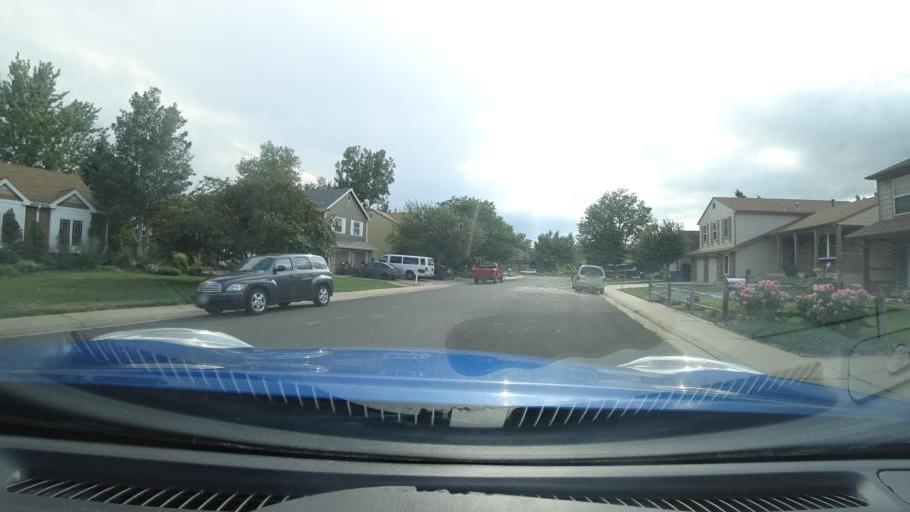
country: US
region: Colorado
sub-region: Adams County
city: Aurora
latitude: 39.6889
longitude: -104.8028
